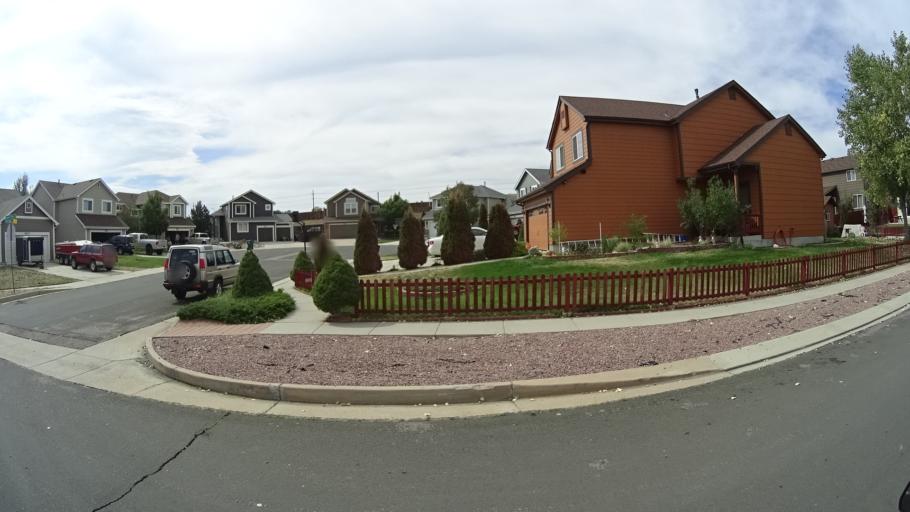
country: US
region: Colorado
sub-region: El Paso County
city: Cimarron Hills
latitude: 38.9026
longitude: -104.7179
